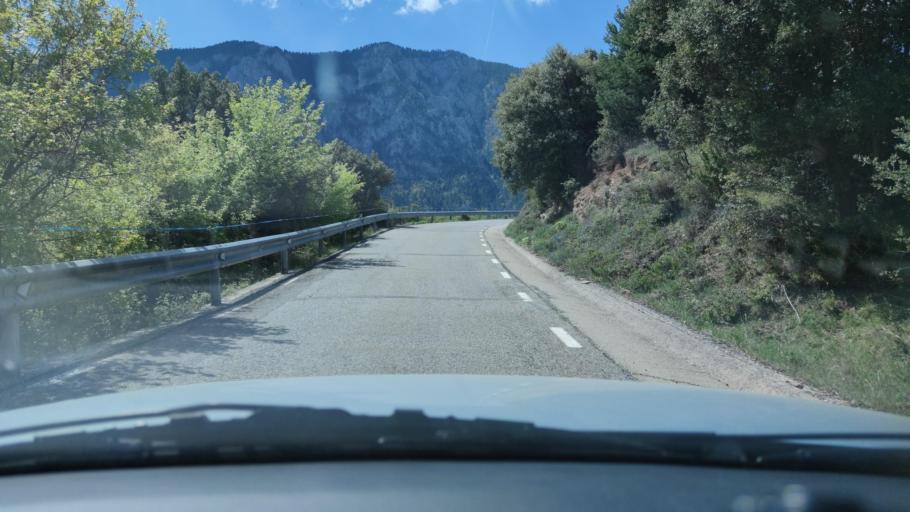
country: ES
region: Catalonia
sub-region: Provincia de Lleida
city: Coll de Nargo
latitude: 42.2980
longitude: 1.2760
